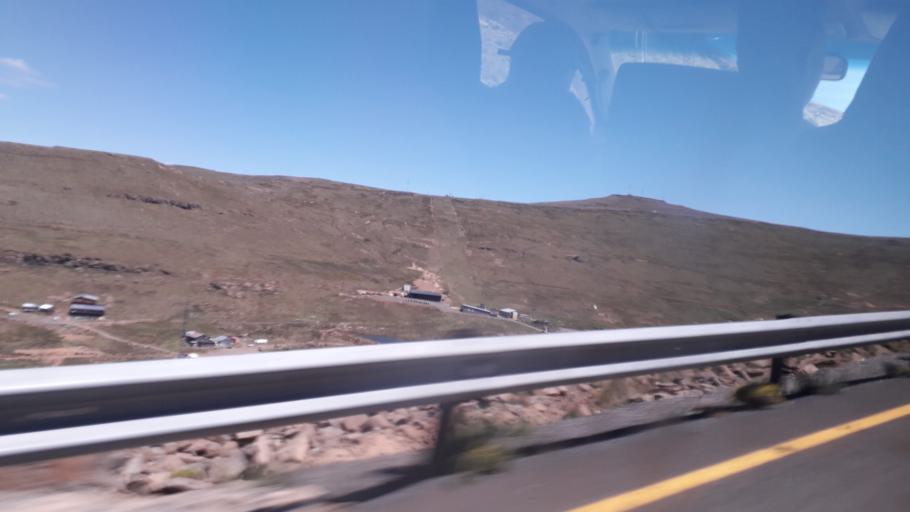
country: ZA
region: Orange Free State
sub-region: Thabo Mofutsanyana District Municipality
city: Phuthaditjhaba
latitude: -28.8276
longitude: 28.7302
